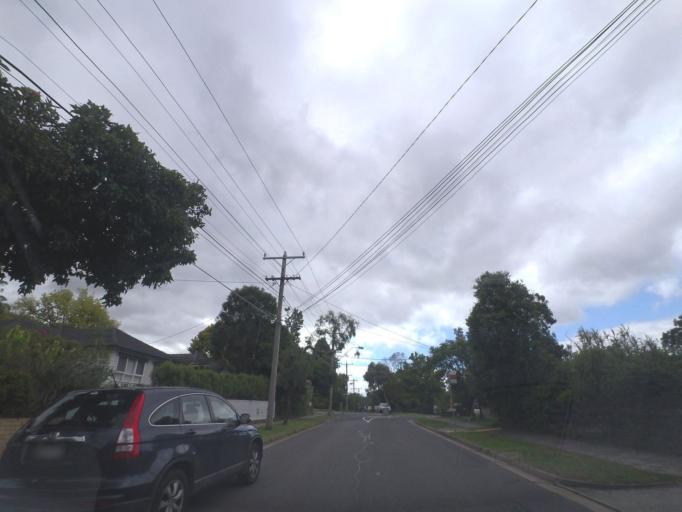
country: AU
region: Victoria
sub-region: Whitehorse
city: Vermont
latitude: -37.8311
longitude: 145.2088
